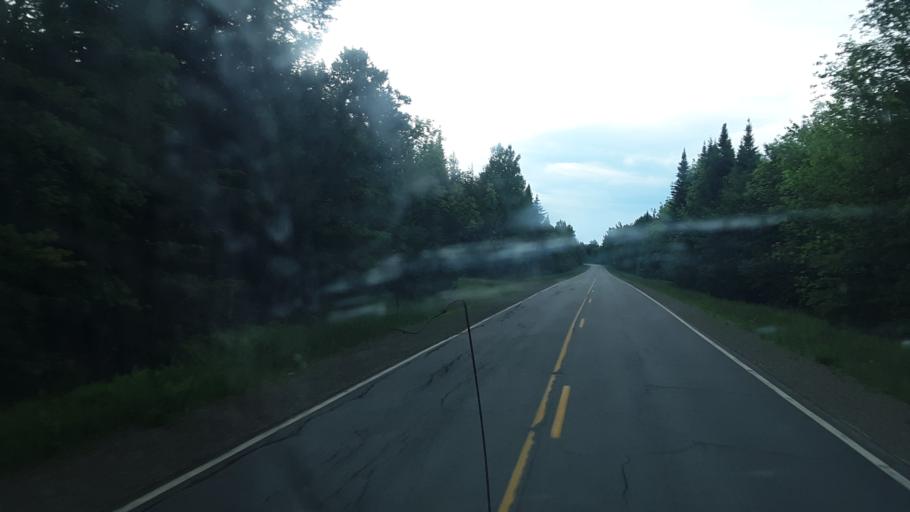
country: US
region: Maine
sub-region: Penobscot County
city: Medway
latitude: 45.6906
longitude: -68.2830
